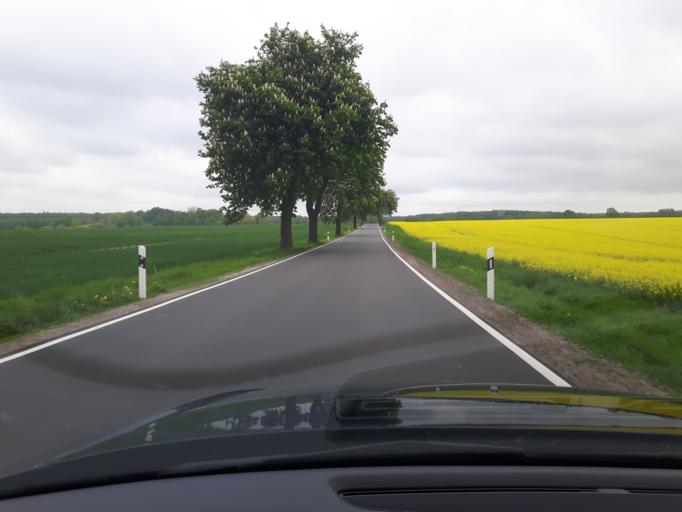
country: DE
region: Mecklenburg-Vorpommern
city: Gnoien
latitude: 53.9851
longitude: 12.6901
